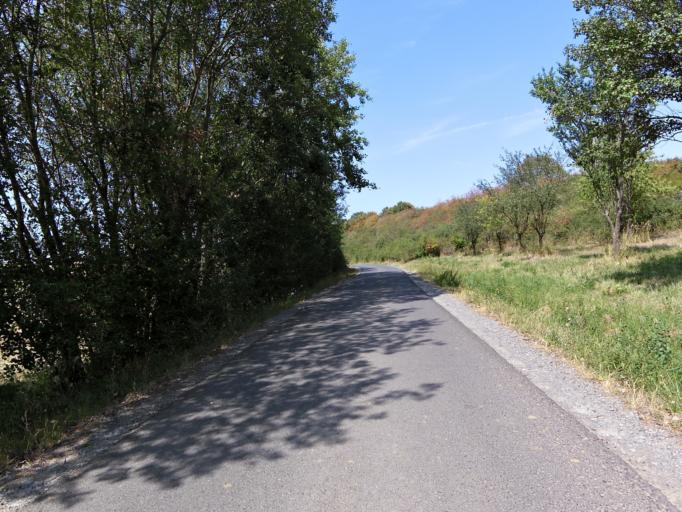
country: DE
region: Bavaria
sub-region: Regierungsbezirk Unterfranken
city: Theilheim
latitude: 49.7684
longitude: 10.0345
